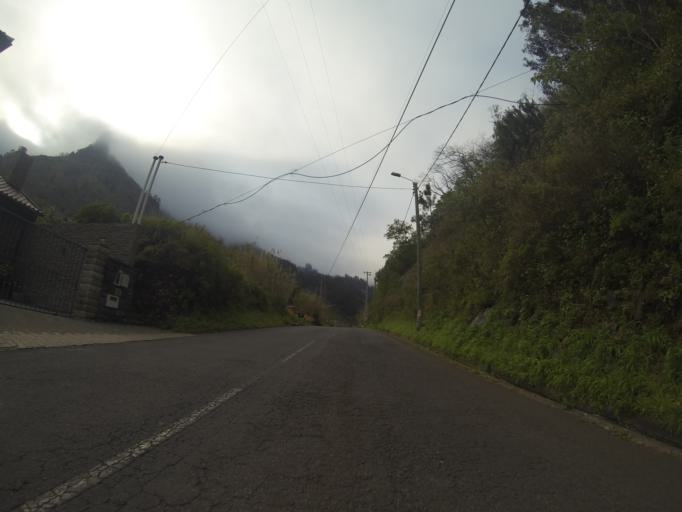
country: PT
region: Madeira
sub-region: Camara de Lobos
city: Curral das Freiras
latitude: 32.7365
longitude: -16.9688
